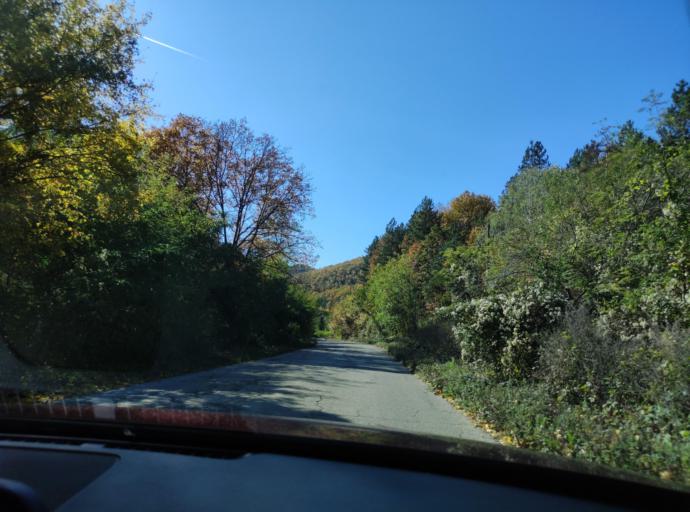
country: BG
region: Montana
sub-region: Obshtina Chiprovtsi
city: Chiprovtsi
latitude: 43.4145
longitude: 22.9444
